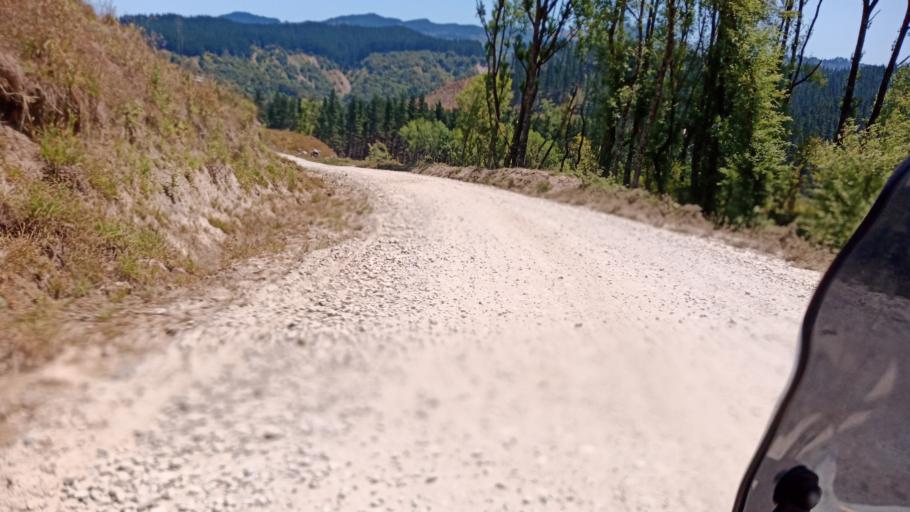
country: NZ
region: Gisborne
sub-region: Gisborne District
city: Gisborne
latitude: -38.2856
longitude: 178.0099
